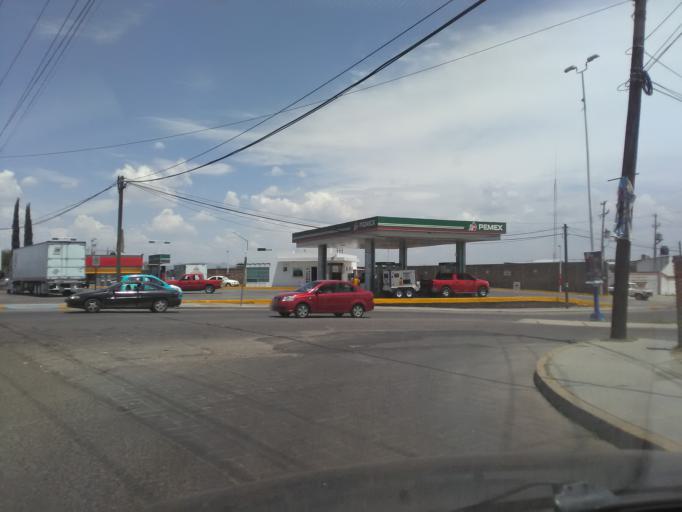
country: MX
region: Durango
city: Victoria de Durango
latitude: 24.0303
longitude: -104.6136
